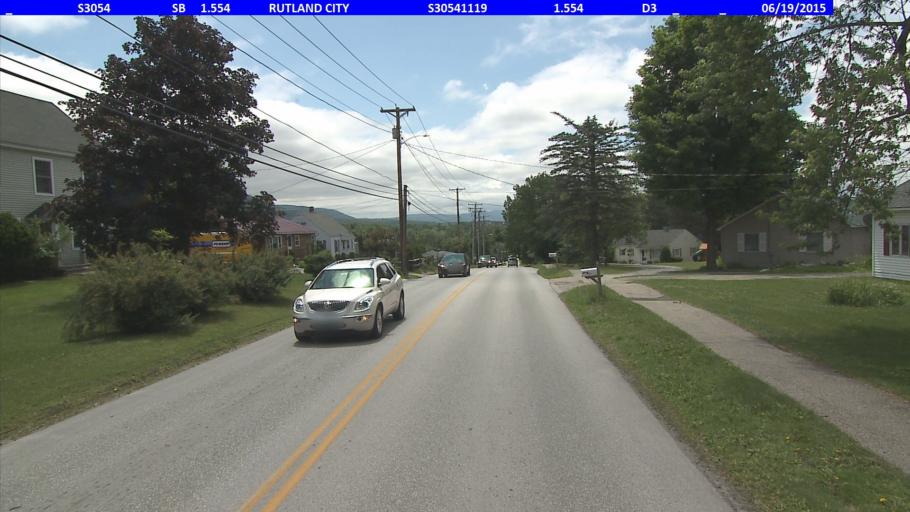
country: US
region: Vermont
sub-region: Rutland County
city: Rutland
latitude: 43.6136
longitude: -72.9567
